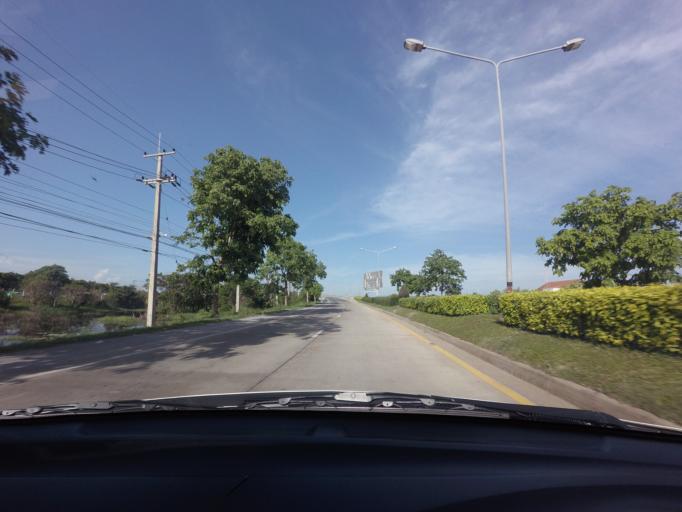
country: TH
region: Suphan Buri
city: Suphan Buri
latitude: 14.4455
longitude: 100.1291
